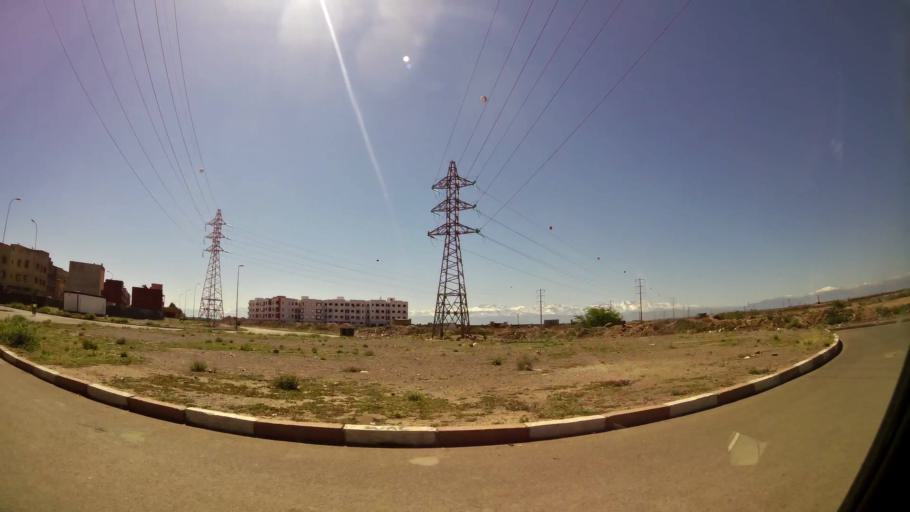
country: MA
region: Marrakech-Tensift-Al Haouz
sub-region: Marrakech
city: Marrakesh
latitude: 31.5706
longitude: -8.0589
